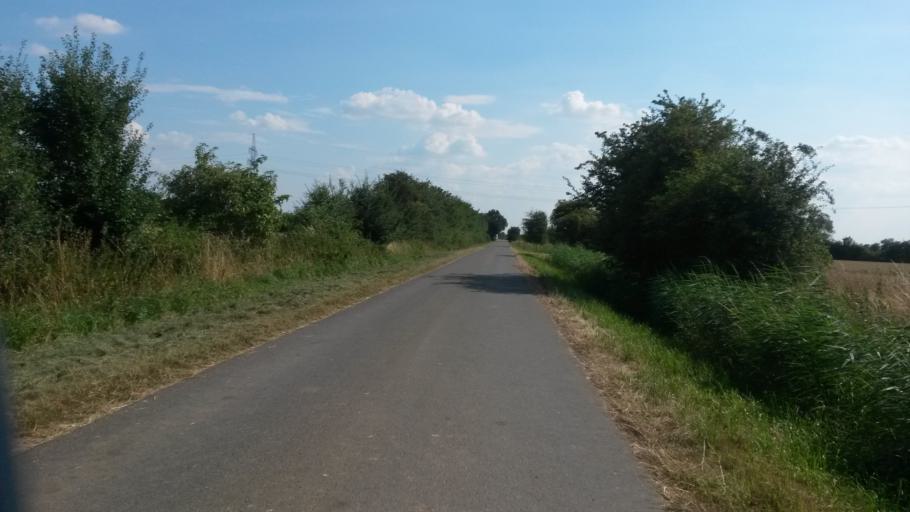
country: DE
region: Lower Saxony
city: Riede
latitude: 53.0217
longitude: 8.9102
